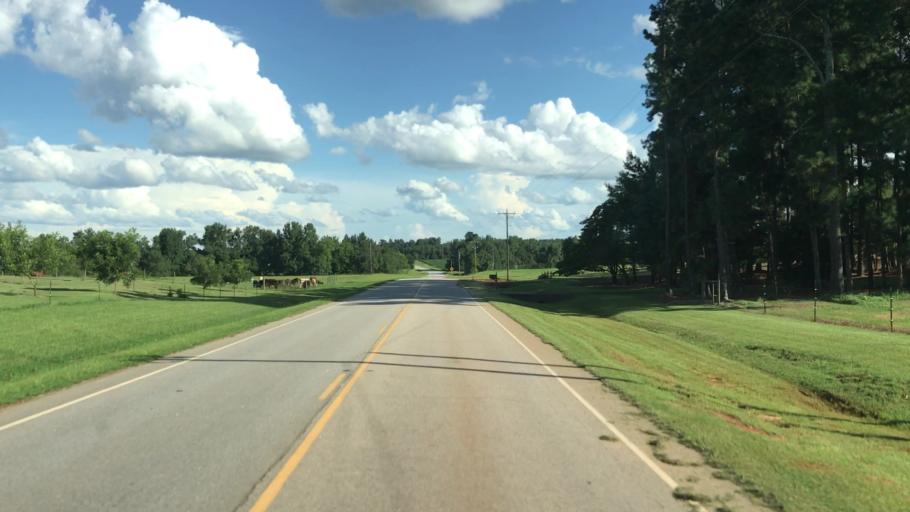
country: US
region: Georgia
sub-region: Jefferson County
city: Wrens
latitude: 33.1353
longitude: -82.4542
